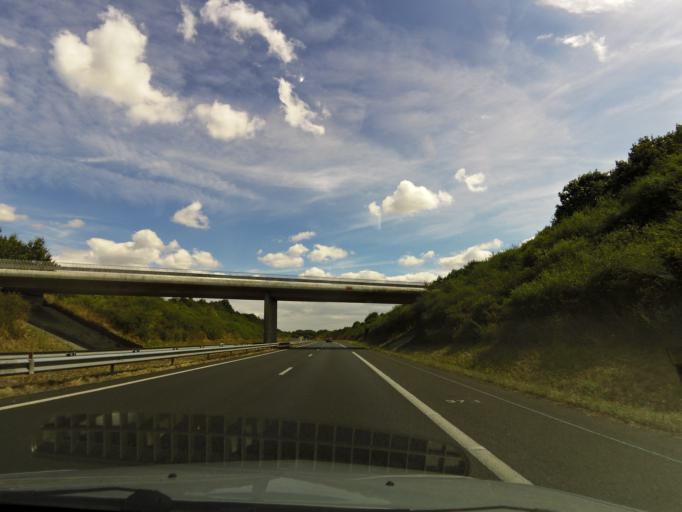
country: FR
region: Pays de la Loire
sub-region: Departement de la Vendee
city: Chauche
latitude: 46.8486
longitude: -1.2701
